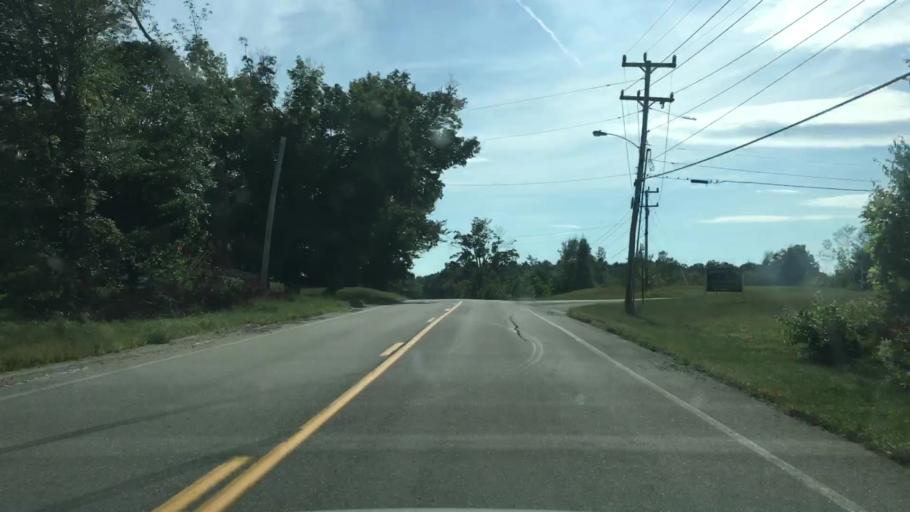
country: US
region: Maine
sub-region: Penobscot County
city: Lincoln
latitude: 45.4068
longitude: -68.5020
